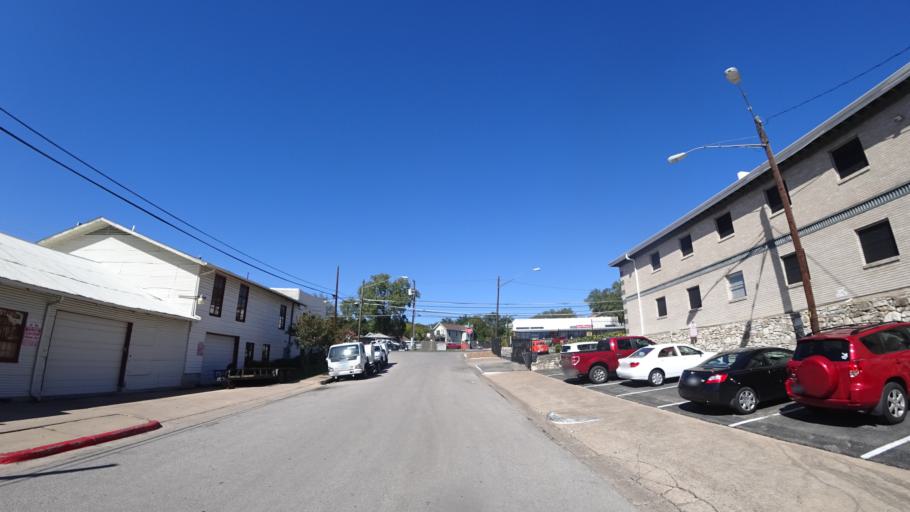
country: US
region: Texas
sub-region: Travis County
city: Austin
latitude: 30.2842
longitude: -97.7170
